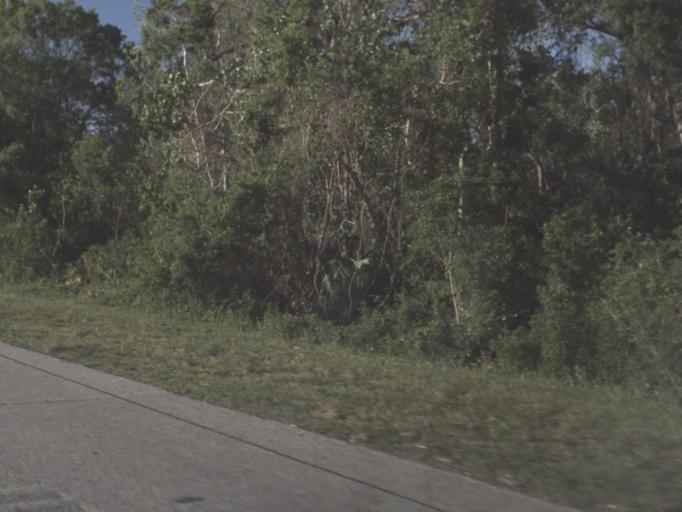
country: US
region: Florida
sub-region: Flagler County
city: Palm Coast
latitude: 29.5691
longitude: -81.2285
